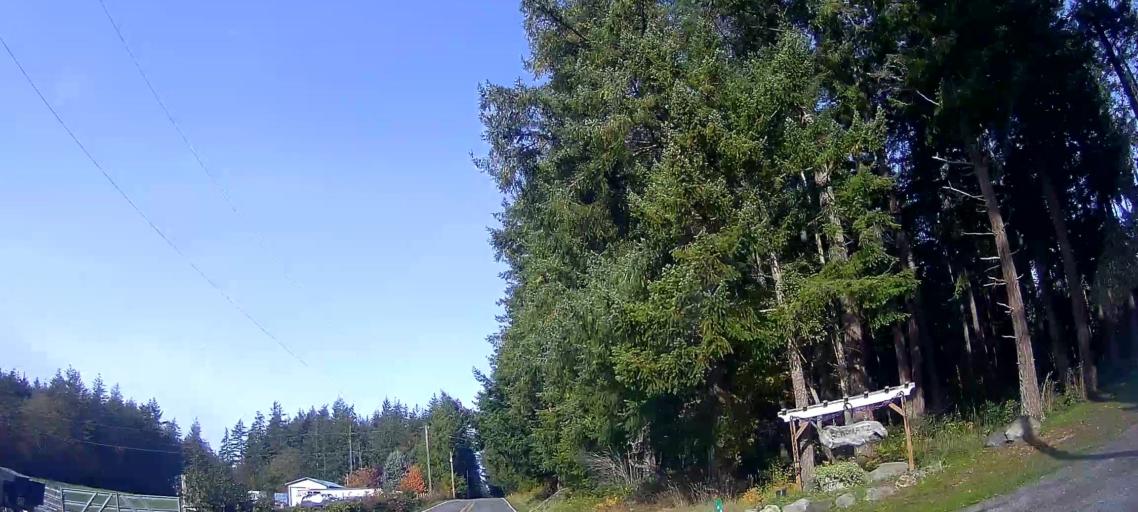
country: US
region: Washington
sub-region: Island County
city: Camano
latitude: 48.2088
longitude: -122.4562
